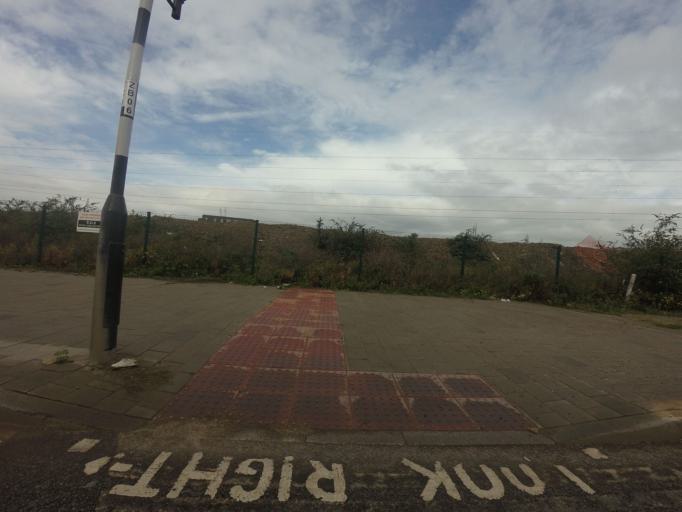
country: GB
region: England
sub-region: Greater London
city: Abbey Wood
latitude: 51.5186
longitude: 0.1130
